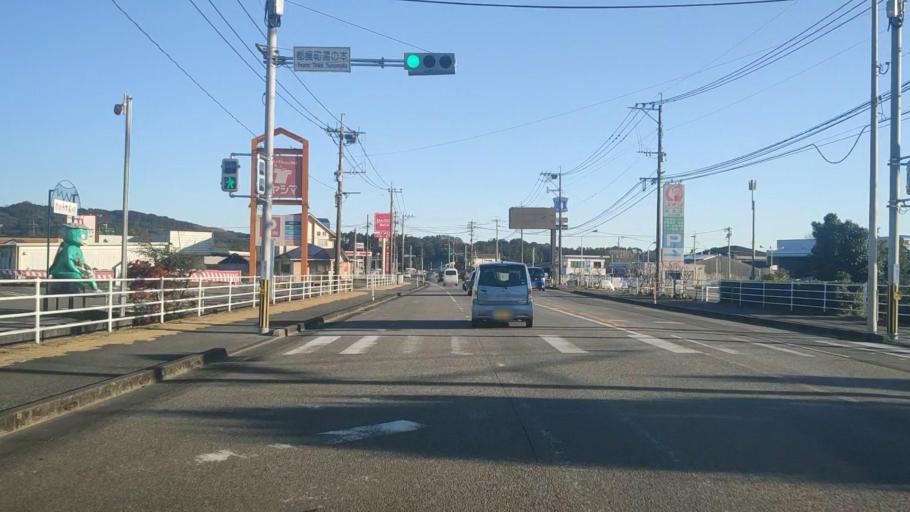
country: JP
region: Miyazaki
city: Takanabe
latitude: 32.2567
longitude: 131.5553
